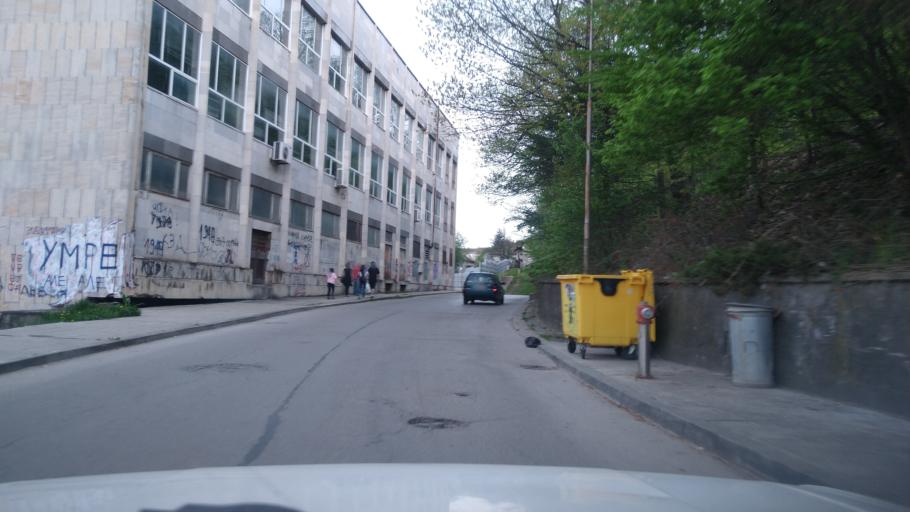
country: BG
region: Gabrovo
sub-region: Obshtina Gabrovo
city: Gabrovo
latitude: 42.8664
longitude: 25.3166
